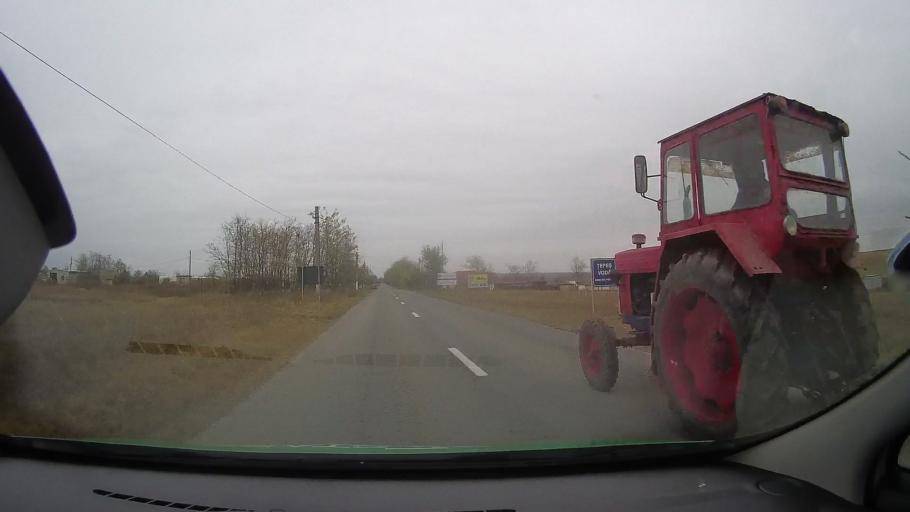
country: RO
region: Constanta
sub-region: Comuna Silistea
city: Silistea
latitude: 44.4400
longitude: 28.2299
